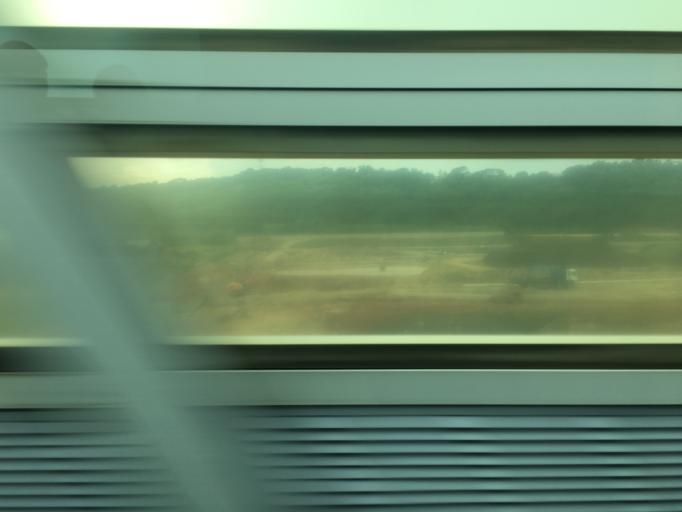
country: TW
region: Taiwan
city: Taoyuan City
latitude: 25.0808
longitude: 121.2910
